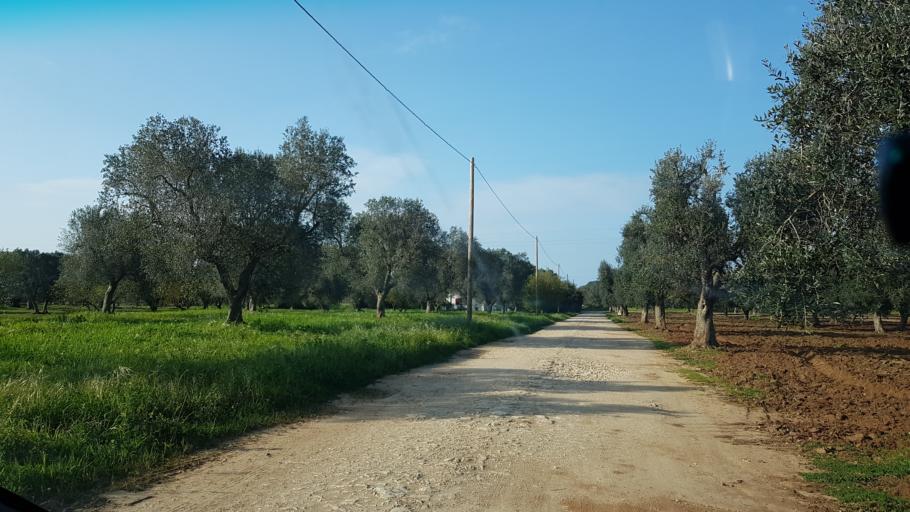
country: IT
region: Apulia
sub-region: Provincia di Brindisi
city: San Vito dei Normanni
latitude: 40.6667
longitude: 17.7934
